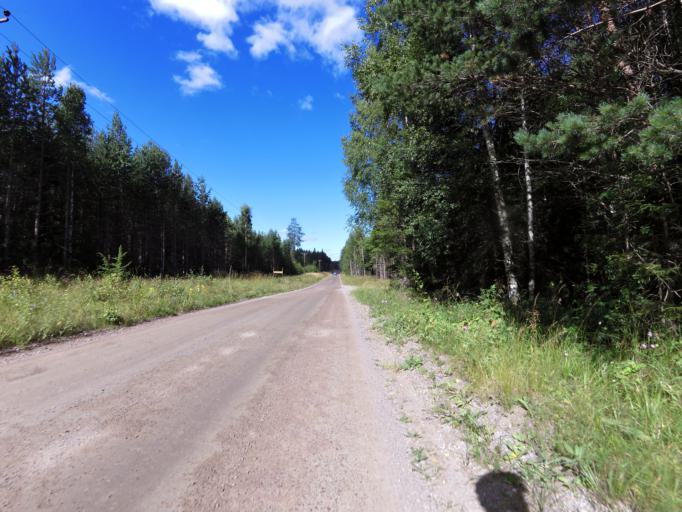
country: SE
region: Gaevleborg
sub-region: Hofors Kommun
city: Hofors
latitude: 60.5054
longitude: 16.3153
